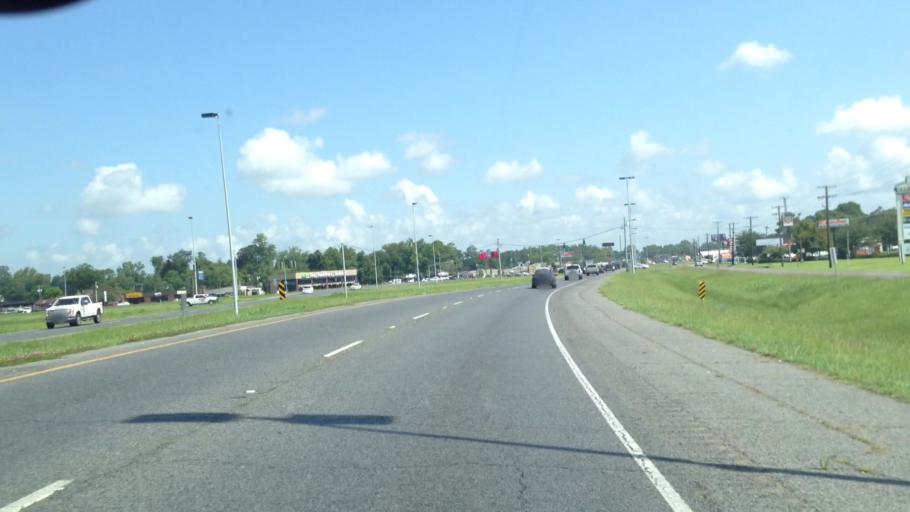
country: US
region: Louisiana
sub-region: Rapides Parish
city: Alexandria
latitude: 31.2975
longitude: -92.4794
